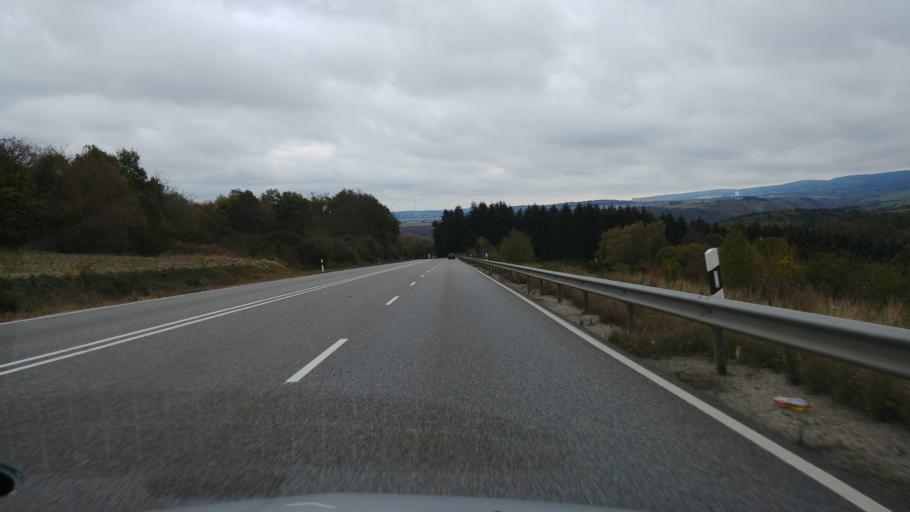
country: DE
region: Rheinland-Pfalz
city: Immert
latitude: 49.7702
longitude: 7.0222
